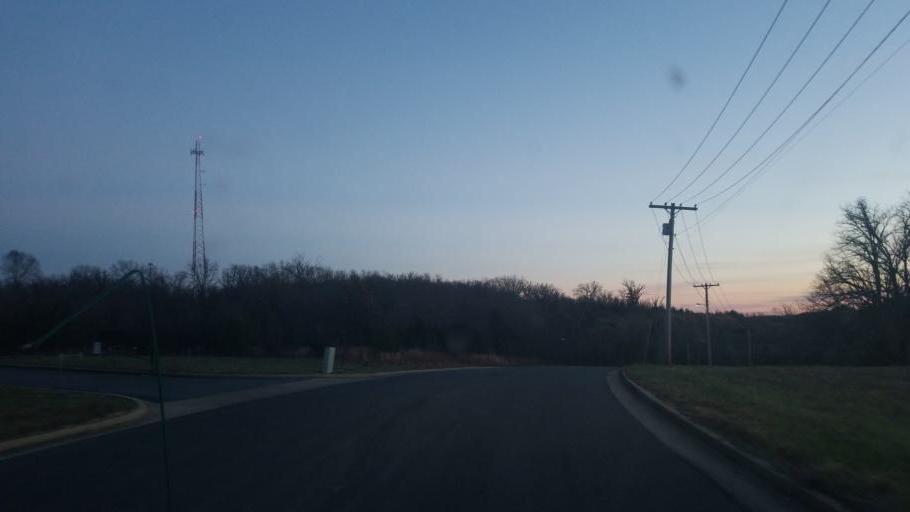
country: US
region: Missouri
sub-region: Howell County
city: West Plains
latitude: 36.7275
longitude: -91.8758
